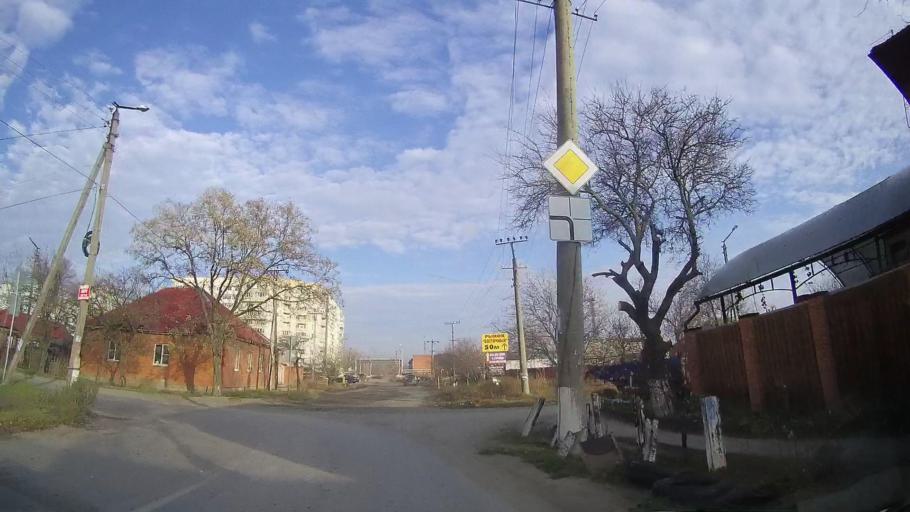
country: RU
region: Rostov
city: Bataysk
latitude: 47.1335
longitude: 39.7737
